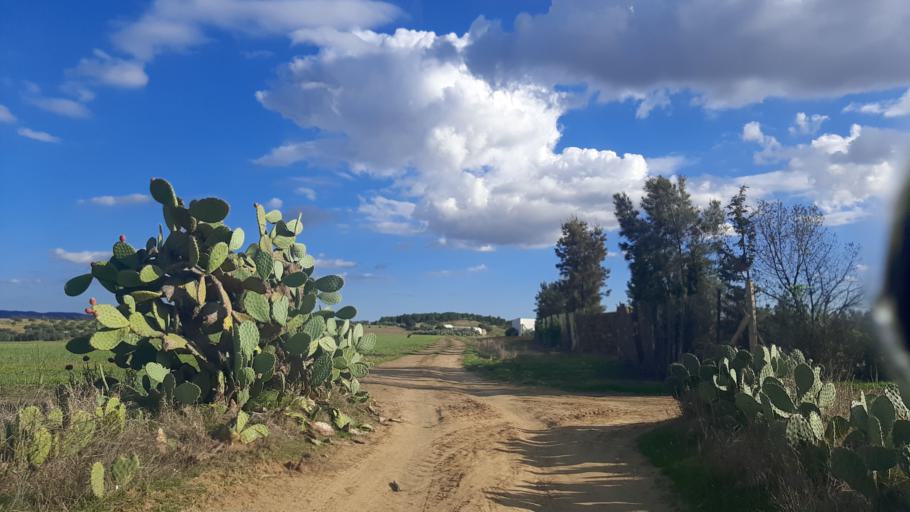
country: TN
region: Nabul
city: Bu `Urqub
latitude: 36.4626
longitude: 10.4855
